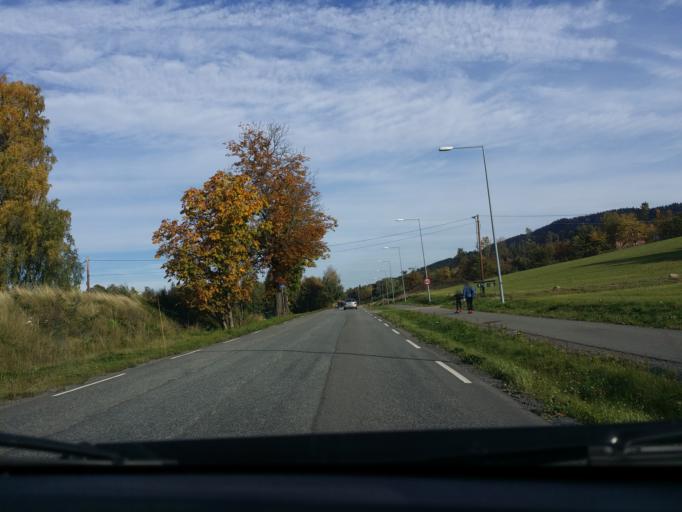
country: NO
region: Buskerud
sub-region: Lier
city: Tranby
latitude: 59.8193
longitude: 10.2527
